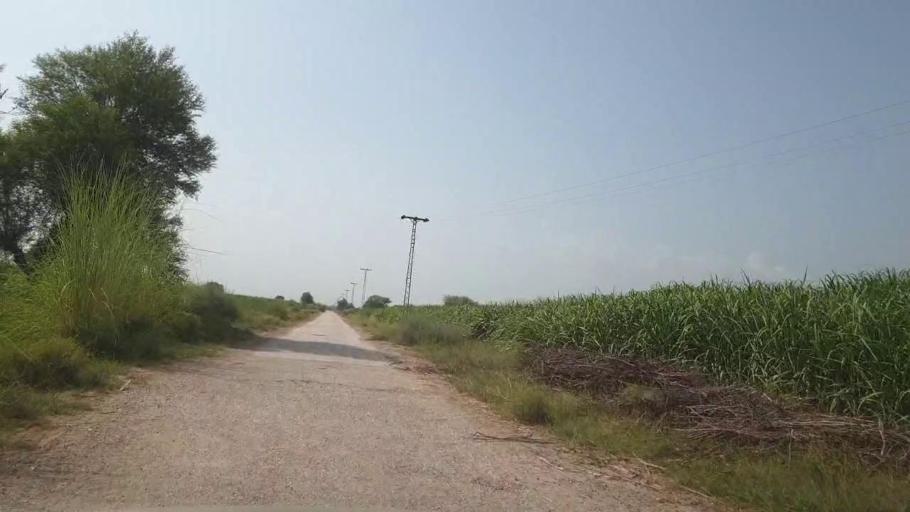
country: PK
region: Sindh
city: Pano Aqil
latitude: 27.7829
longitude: 69.1597
